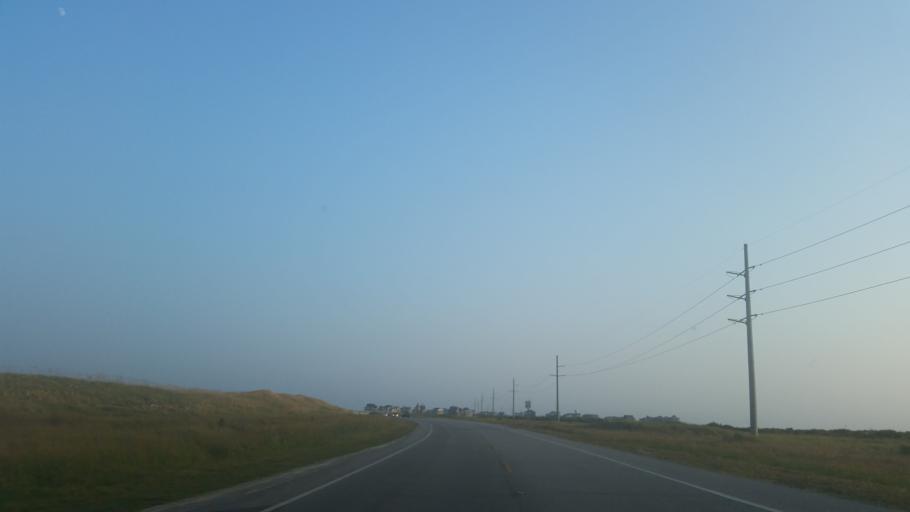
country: US
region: North Carolina
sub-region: Dare County
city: Wanchese
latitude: 35.6159
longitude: -75.4680
